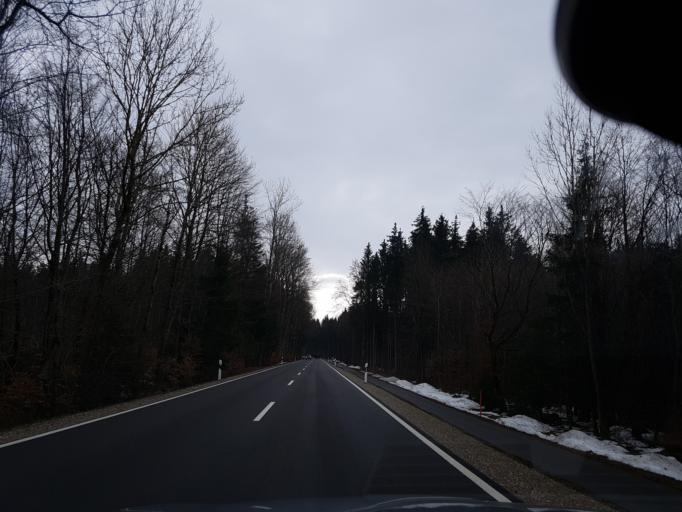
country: DE
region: Bavaria
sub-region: Upper Bavaria
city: Hohenkirchen-Siegertsbrunn
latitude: 48.0016
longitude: 11.7068
